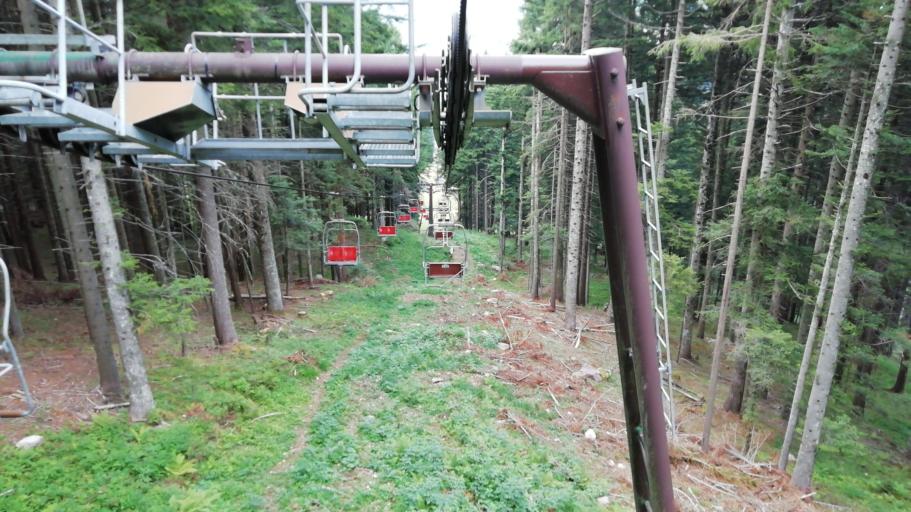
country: IT
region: Trentino-Alto Adige
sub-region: Provincia di Trento
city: Folgaria
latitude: 45.9006
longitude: 11.1908
